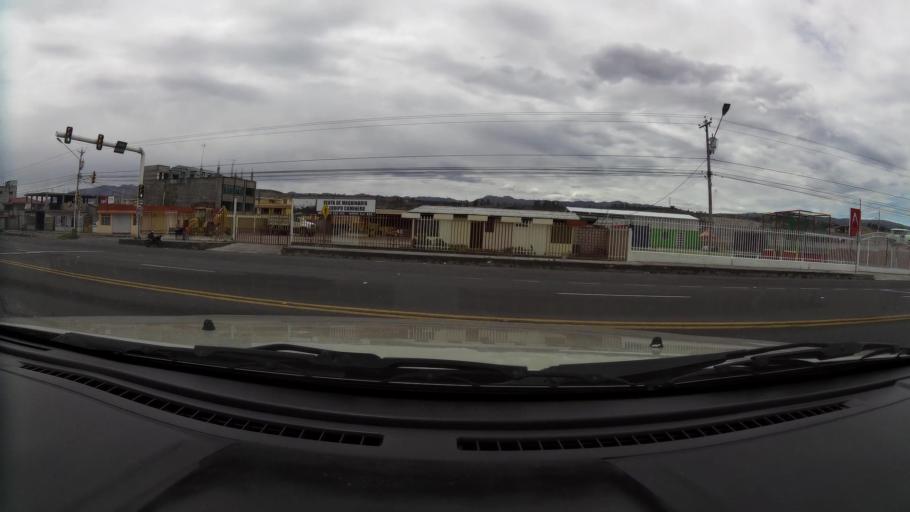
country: EC
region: Cotopaxi
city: Latacunga
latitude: -0.9660
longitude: -78.6110
